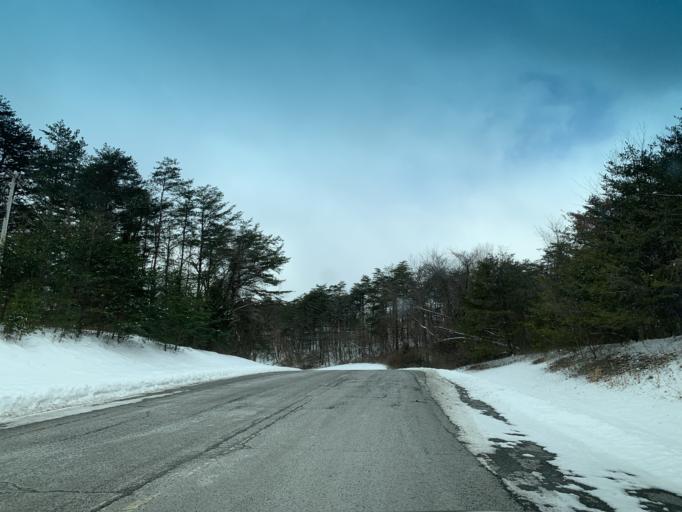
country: US
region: West Virginia
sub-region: Morgan County
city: Berkeley Springs
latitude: 39.6667
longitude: -78.4395
